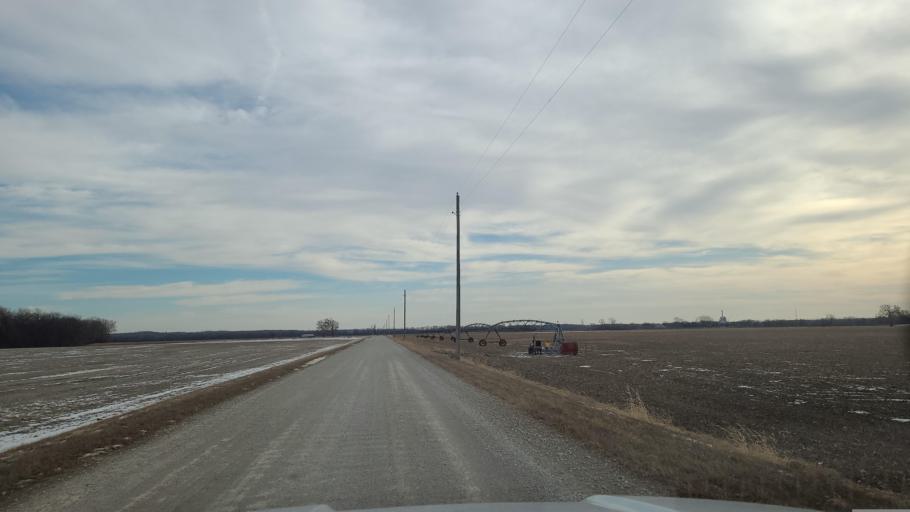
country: US
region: Kansas
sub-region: Douglas County
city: Lawrence
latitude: 39.0297
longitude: -95.3225
